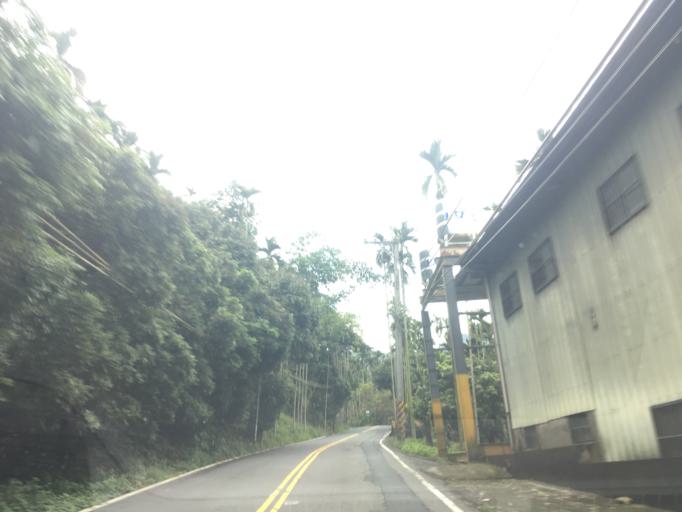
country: TW
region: Taiwan
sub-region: Yunlin
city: Douliu
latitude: 23.5675
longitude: 120.5707
